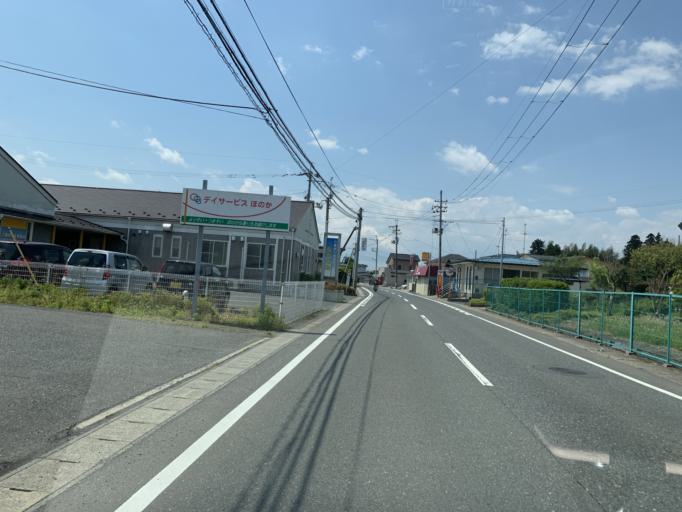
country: JP
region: Miyagi
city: Kogota
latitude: 38.5811
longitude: 141.0335
